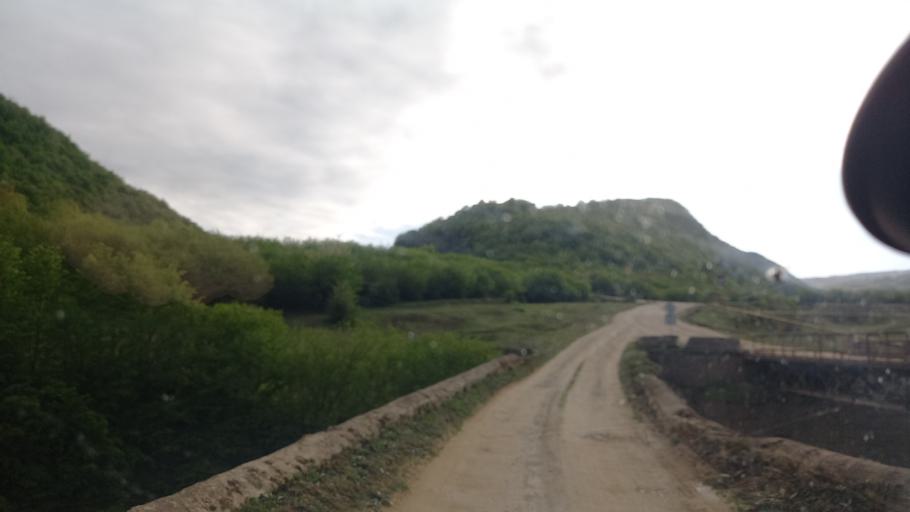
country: RU
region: Dagestan
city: Khuchni
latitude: 41.9614
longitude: 47.8652
